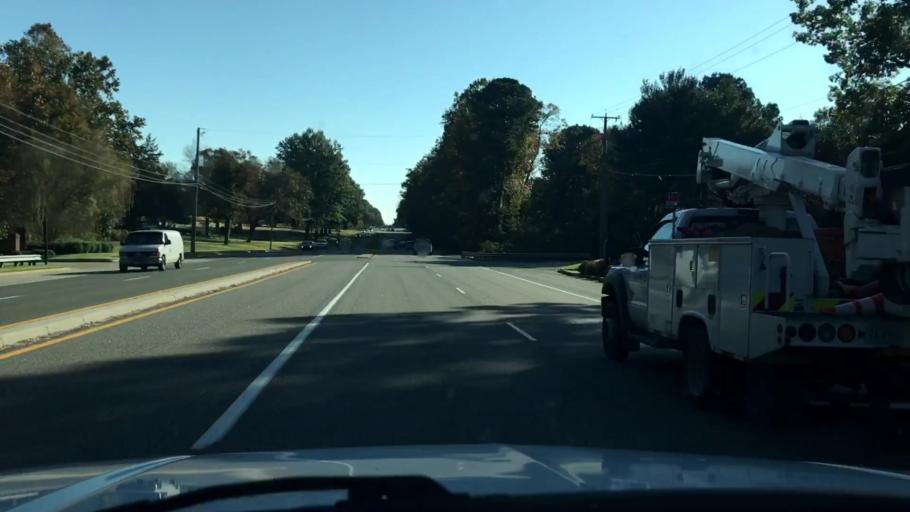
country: US
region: Virginia
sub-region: Henrico County
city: Tuckahoe
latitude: 37.5966
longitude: -77.6010
